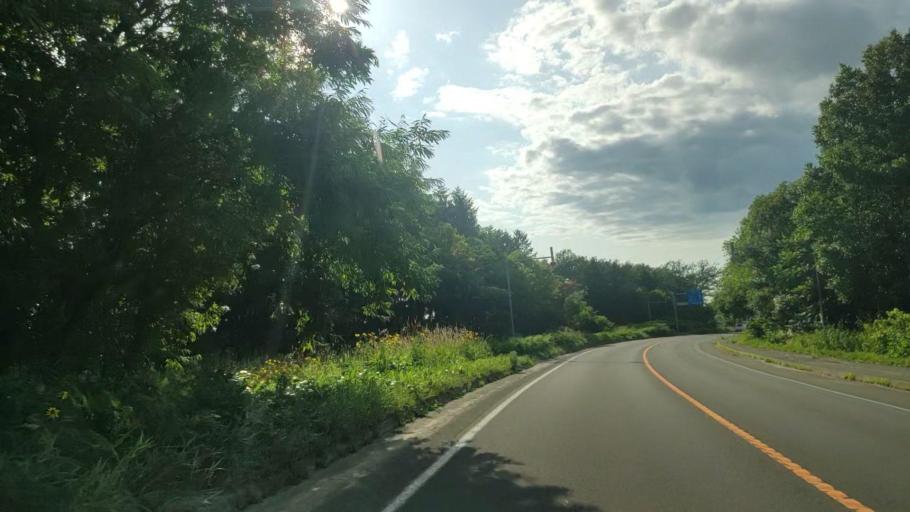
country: JP
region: Hokkaido
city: Makubetsu
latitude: 44.8970
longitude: 141.9182
